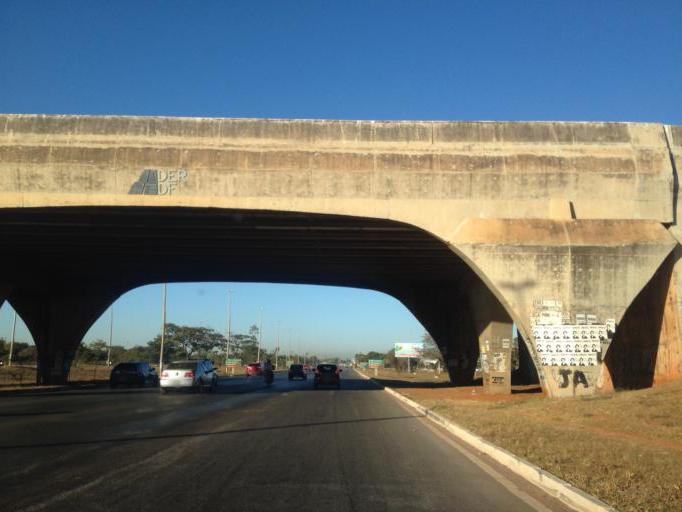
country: BR
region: Federal District
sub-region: Brasilia
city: Brasilia
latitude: -15.7742
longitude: -47.9378
